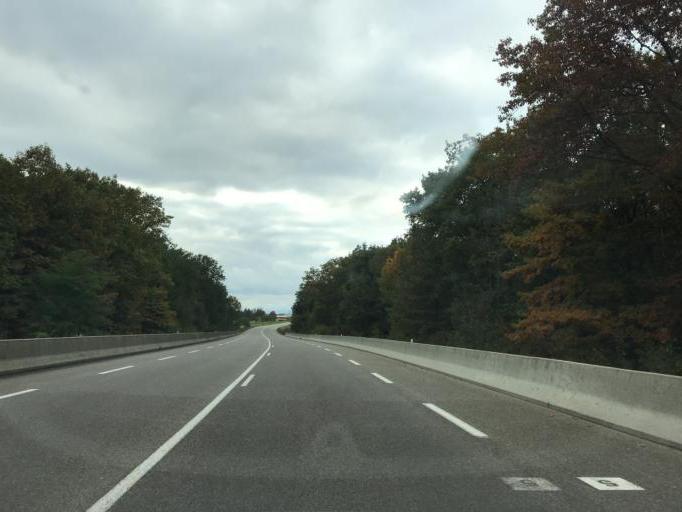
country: FR
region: Rhone-Alpes
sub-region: Departement de l'Ain
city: Bourg-en-Bresse
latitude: 46.2201
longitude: 5.2581
